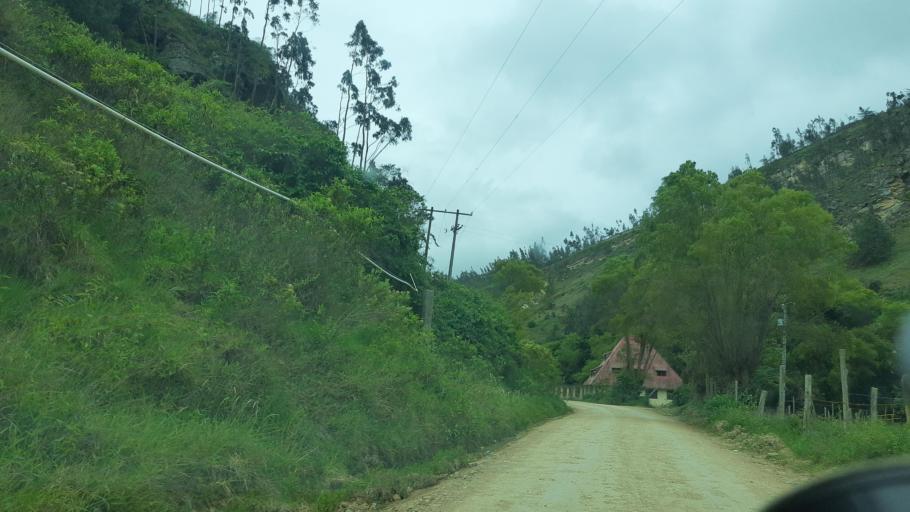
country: CO
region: Boyaca
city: Turmeque
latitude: 5.3241
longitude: -73.4453
